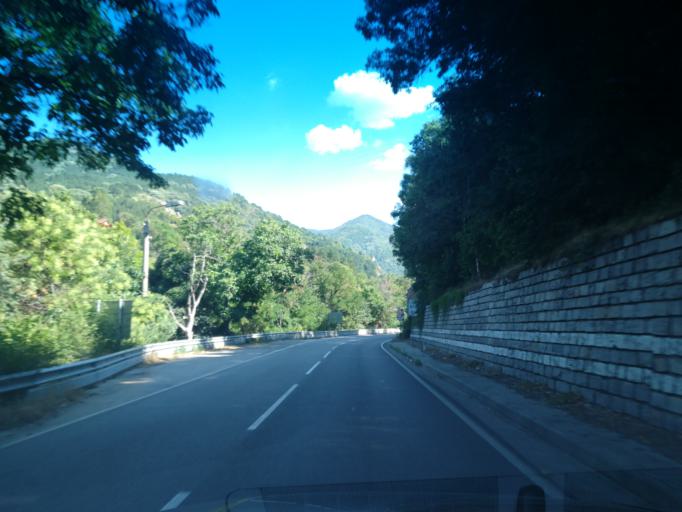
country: BG
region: Plovdiv
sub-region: Obshtina Asenovgrad
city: Asenovgrad
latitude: 41.9986
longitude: 24.8725
